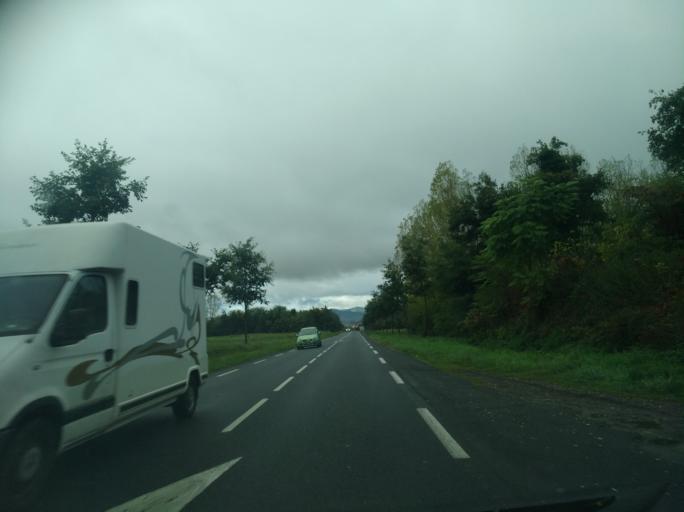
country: FR
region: Rhone-Alpes
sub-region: Departement de l'Ain
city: Guereins
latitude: 46.0989
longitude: 4.7814
